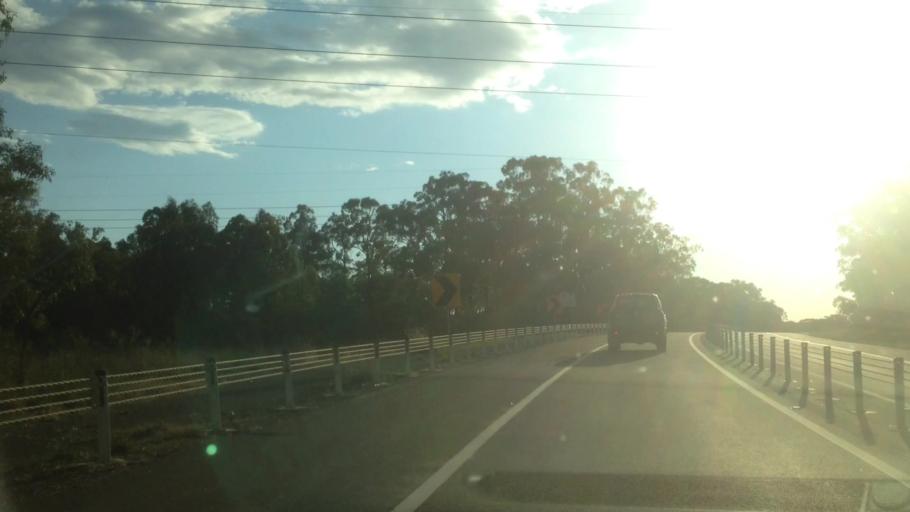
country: AU
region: New South Wales
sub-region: Cessnock
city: Heddon Greta
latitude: -32.8306
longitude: 151.5095
